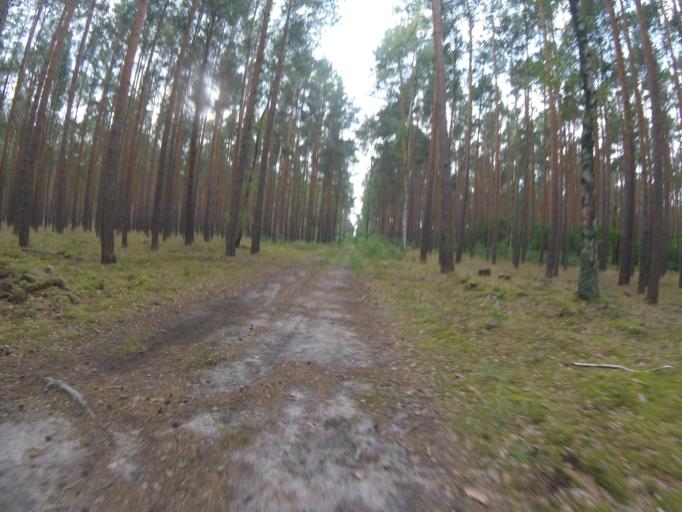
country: DE
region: Brandenburg
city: Schwerin
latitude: 52.1864
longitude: 13.6090
